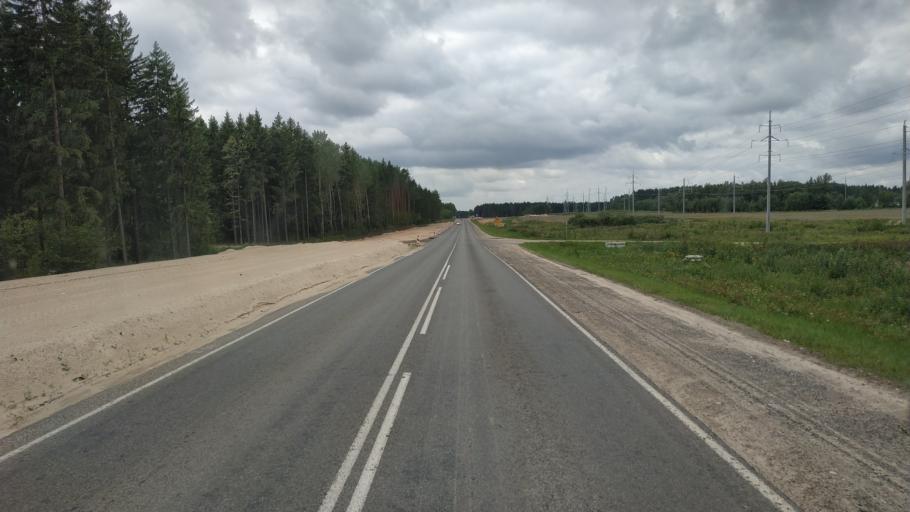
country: BY
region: Mogilev
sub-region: Mahilyowski Rayon
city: Veyno
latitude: 53.8735
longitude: 30.4423
